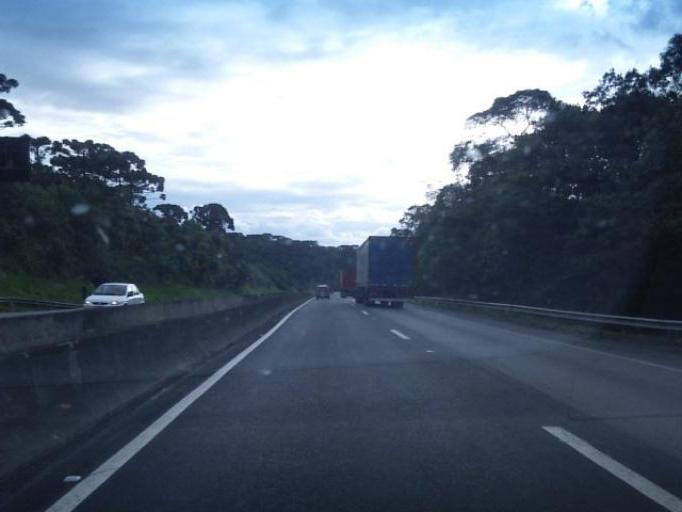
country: BR
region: Parana
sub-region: Campina Grande Do Sul
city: Campina Grande do Sul
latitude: -25.3081
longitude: -48.9990
